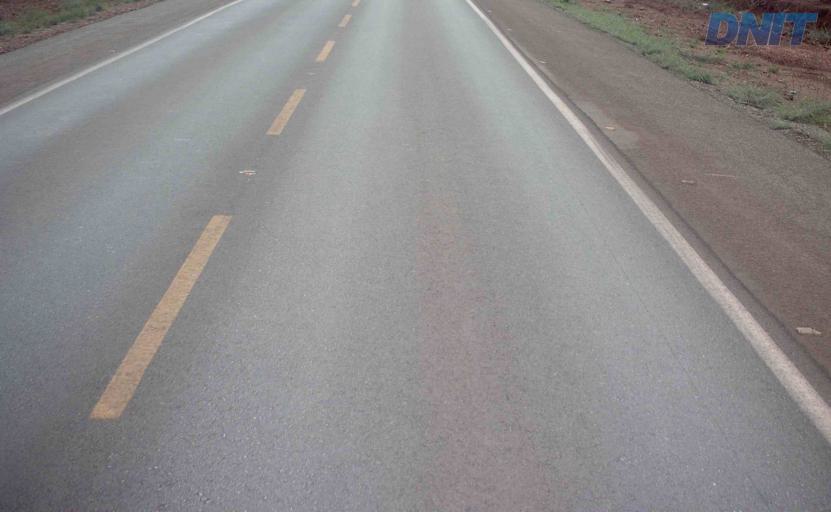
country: BR
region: Goias
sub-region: Barro Alto
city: Barro Alto
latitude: -14.9027
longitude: -48.9631
